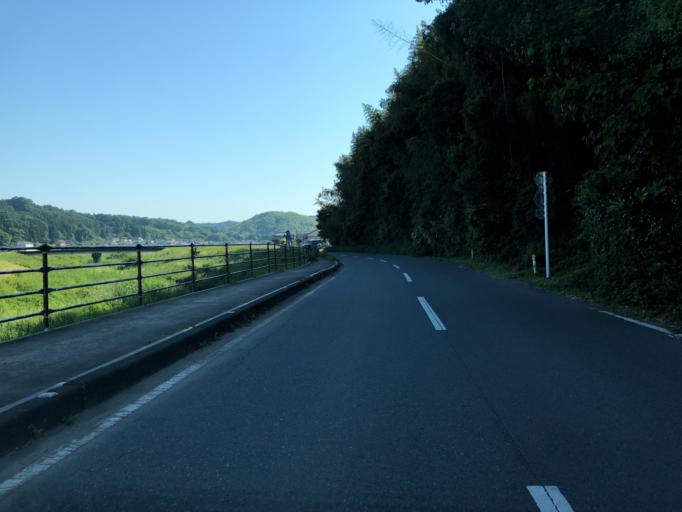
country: JP
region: Ibaraki
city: Kitaibaraki
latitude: 36.8885
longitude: 140.7536
